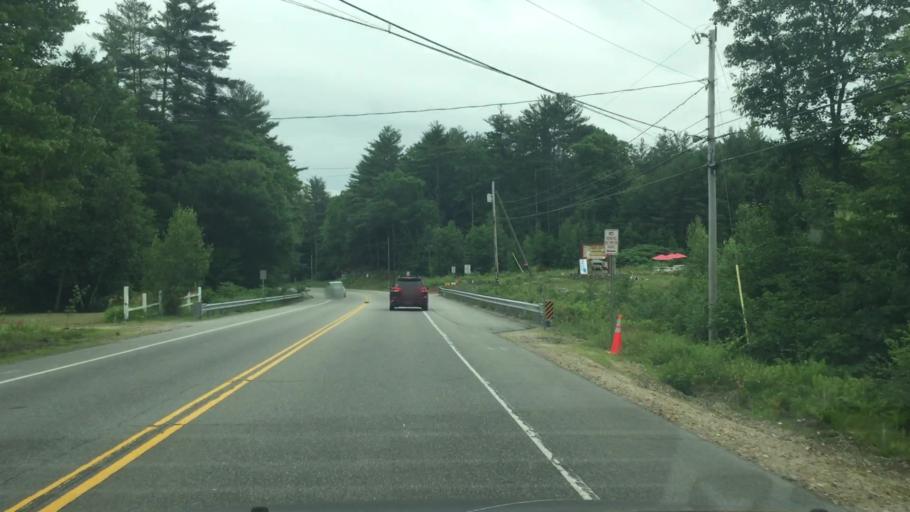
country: US
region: New Hampshire
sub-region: Grafton County
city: Ashland
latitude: 43.6238
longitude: -71.6150
